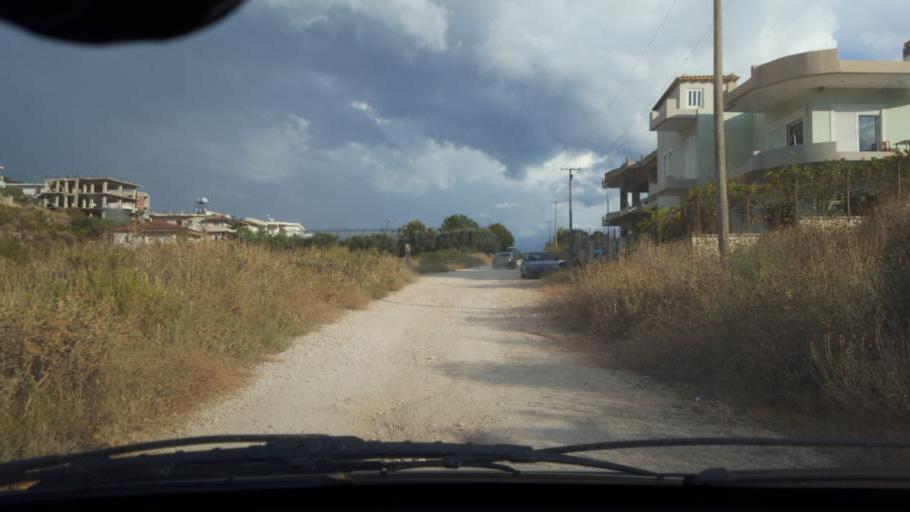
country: AL
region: Vlore
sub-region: Rrethi i Sarandes
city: Sarande
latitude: 39.8419
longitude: 20.0209
